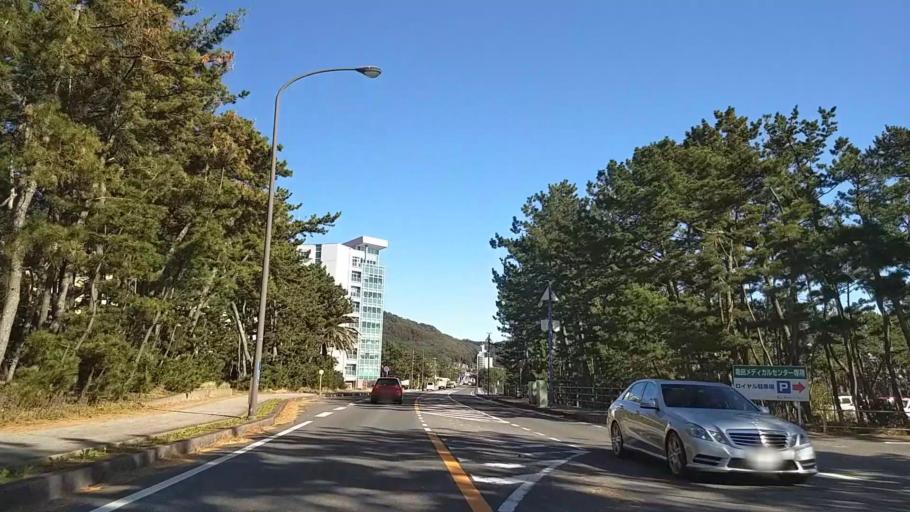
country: JP
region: Chiba
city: Kawaguchi
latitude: 35.1187
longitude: 140.1243
